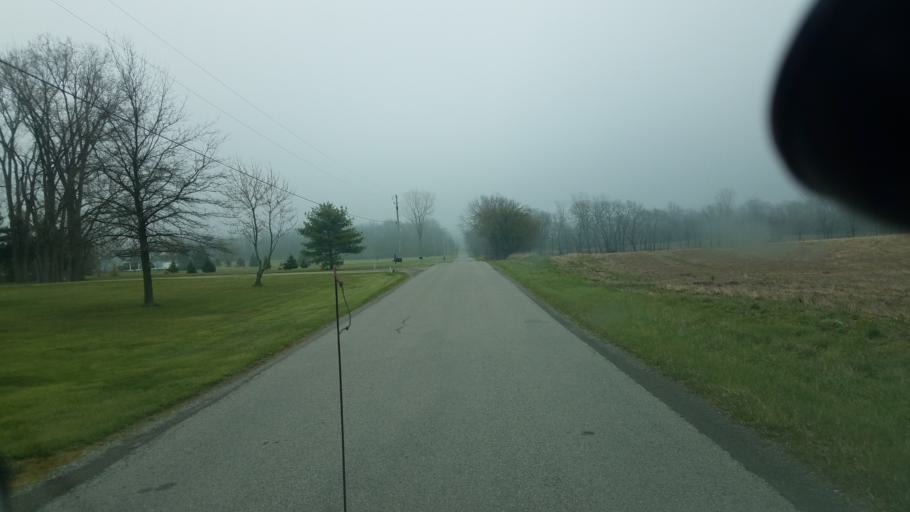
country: US
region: Ohio
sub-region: Logan County
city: Northwood
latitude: 40.4299
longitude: -83.7942
